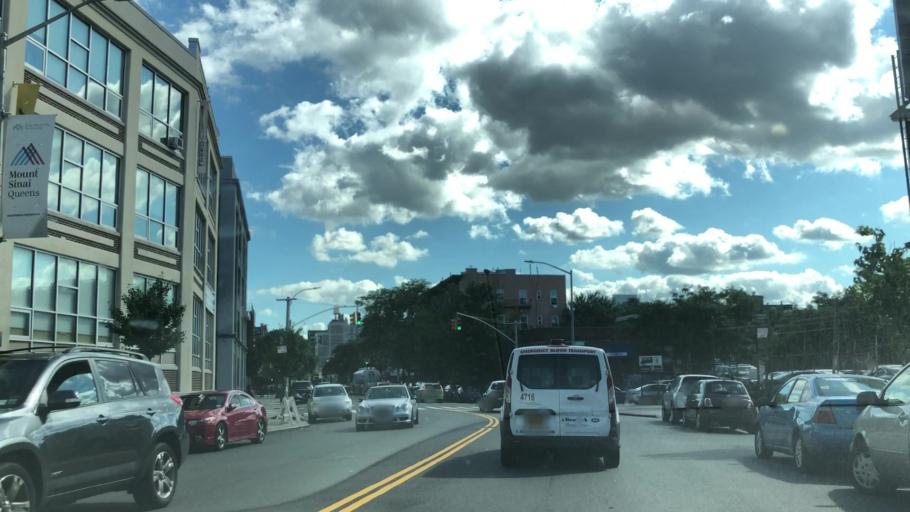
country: US
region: New York
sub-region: Queens County
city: Long Island City
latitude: 40.7493
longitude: -73.9468
